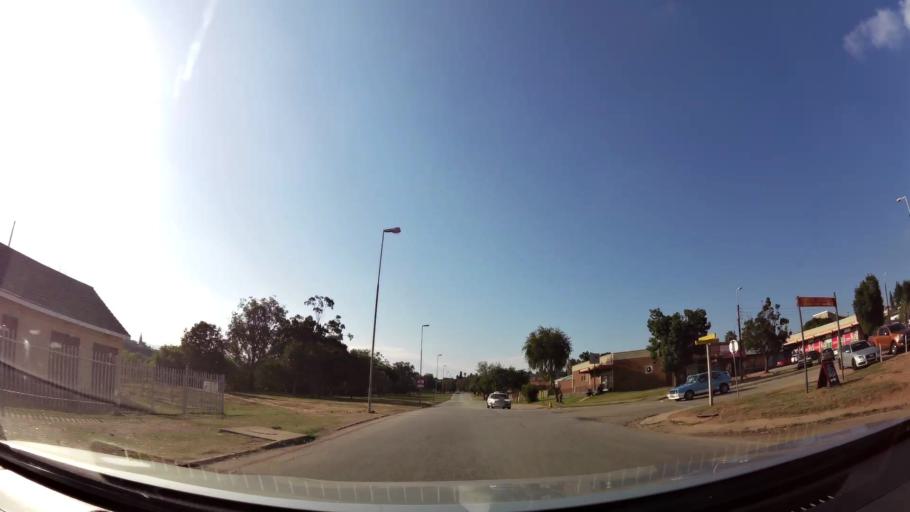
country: ZA
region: Eastern Cape
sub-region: Nelson Mandela Bay Metropolitan Municipality
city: Uitenhage
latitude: -33.7696
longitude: 25.4121
